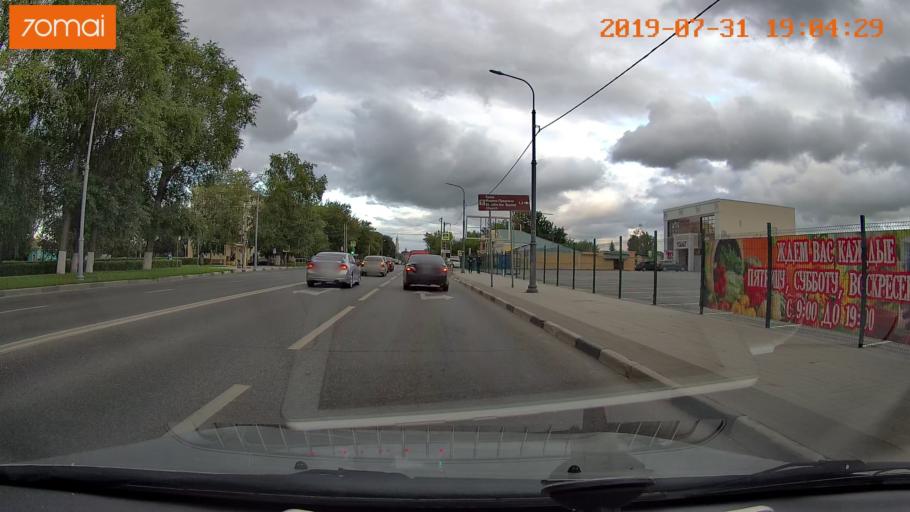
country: RU
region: Moskovskaya
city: Raduzhnyy
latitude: 55.1083
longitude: 38.7411
